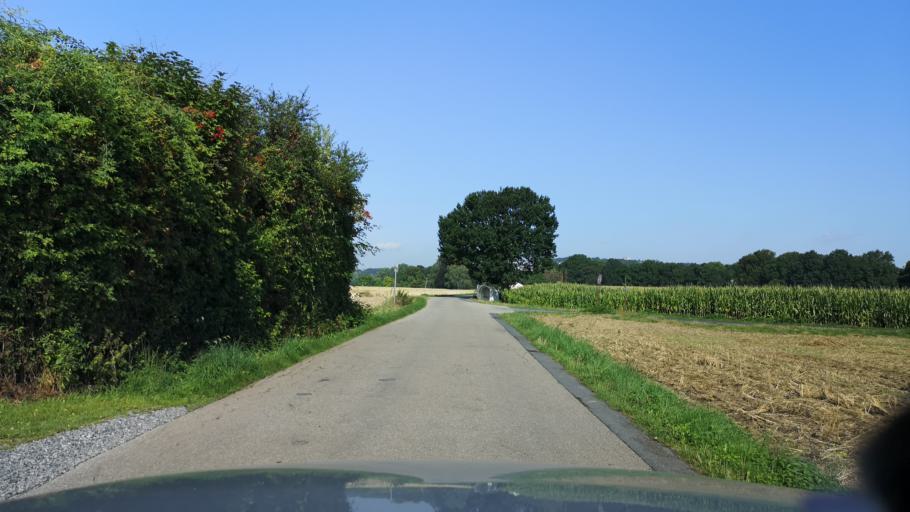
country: DE
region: North Rhine-Westphalia
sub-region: Regierungsbezirk Arnsberg
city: Frondenberg
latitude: 51.4632
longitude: 7.7824
